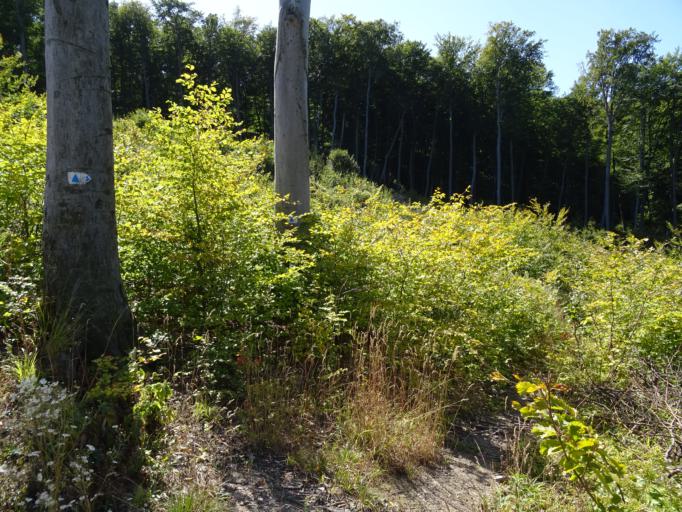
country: HU
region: Fejer
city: Bakonycsernye
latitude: 47.2836
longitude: 18.1089
